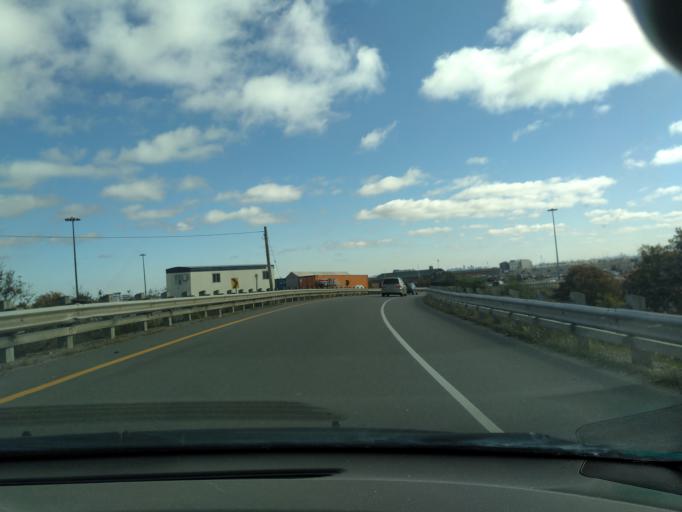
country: CA
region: Ontario
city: Vaughan
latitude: 43.8272
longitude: -79.5485
